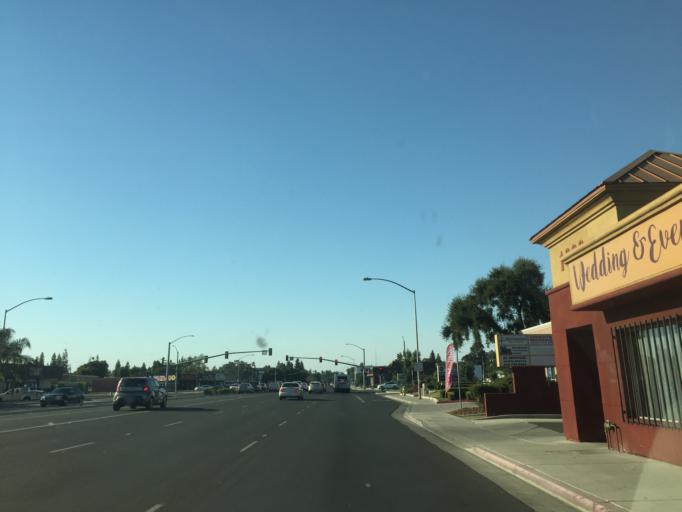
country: US
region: California
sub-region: Tulare County
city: Visalia
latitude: 36.3190
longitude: -119.3138
